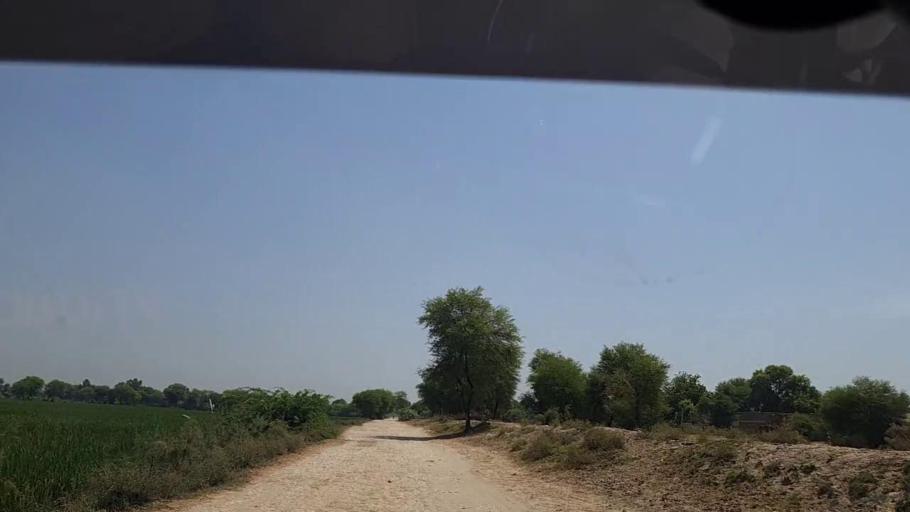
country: PK
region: Sindh
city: Ghauspur
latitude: 28.1696
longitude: 69.1199
